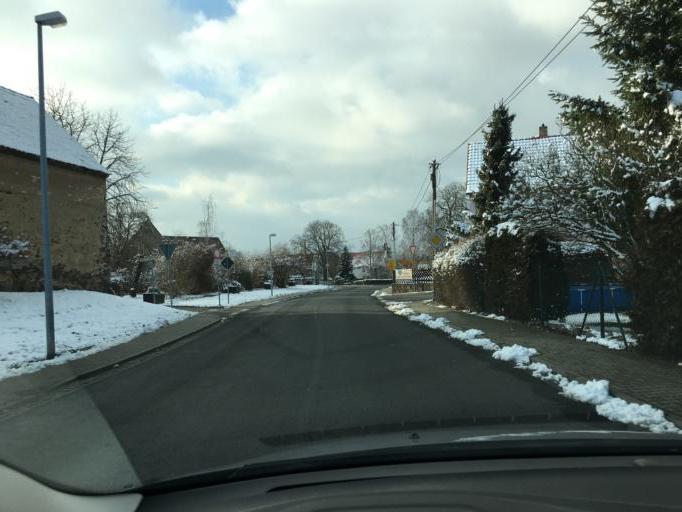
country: DE
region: Saxony
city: Naunhof
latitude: 51.2777
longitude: 12.6433
